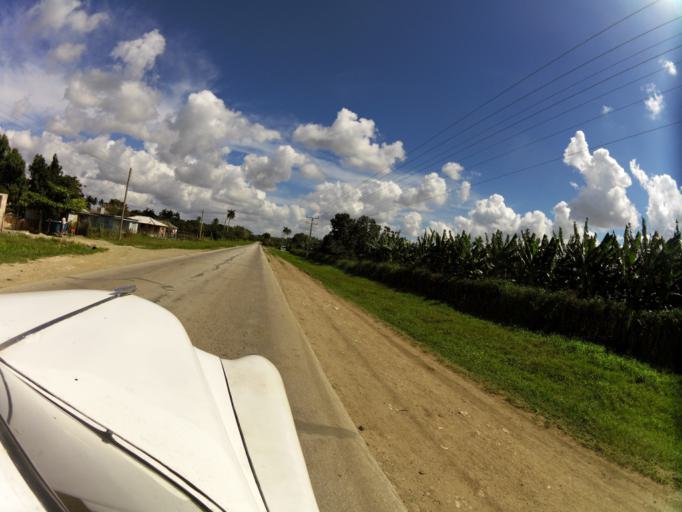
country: CU
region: Holguin
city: Cacocum
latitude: 20.8581
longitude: -76.4568
